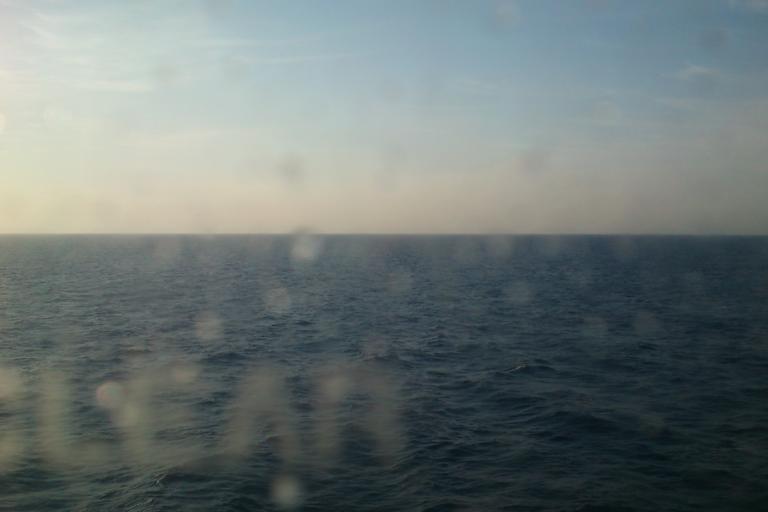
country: JP
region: Ishikawa
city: Nanao
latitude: 37.7634
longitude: 136.4156
